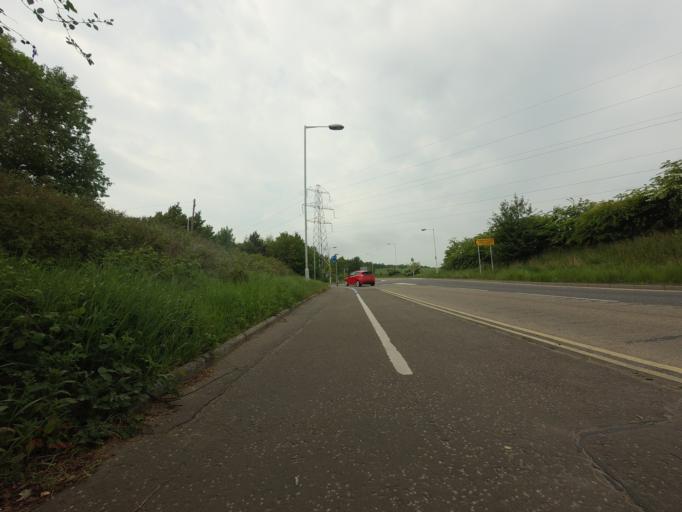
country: GB
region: Scotland
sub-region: Fife
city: Townhill
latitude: 56.0837
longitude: -3.4260
